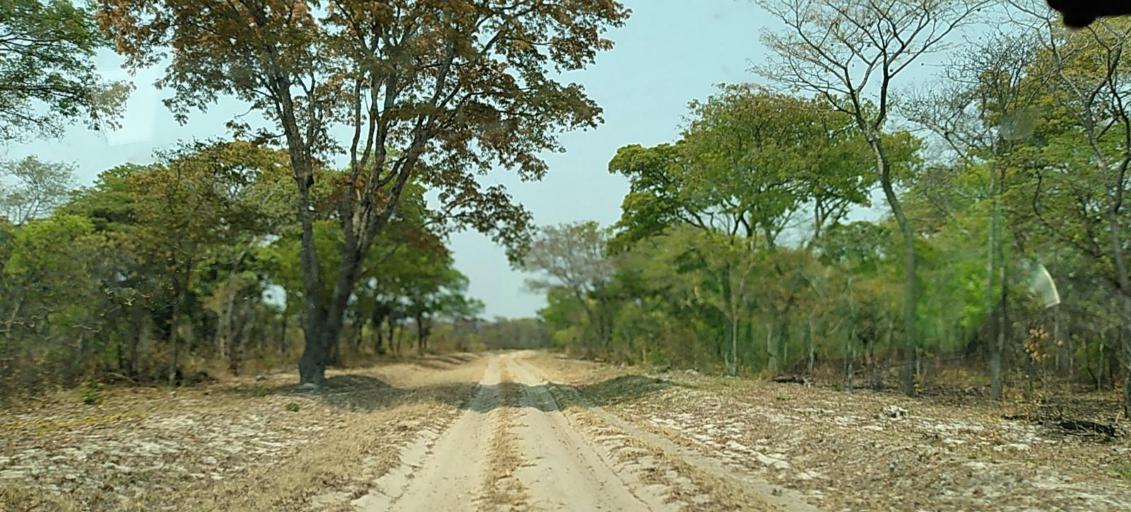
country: ZM
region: North-Western
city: Zambezi
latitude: -13.9329
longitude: 23.2240
